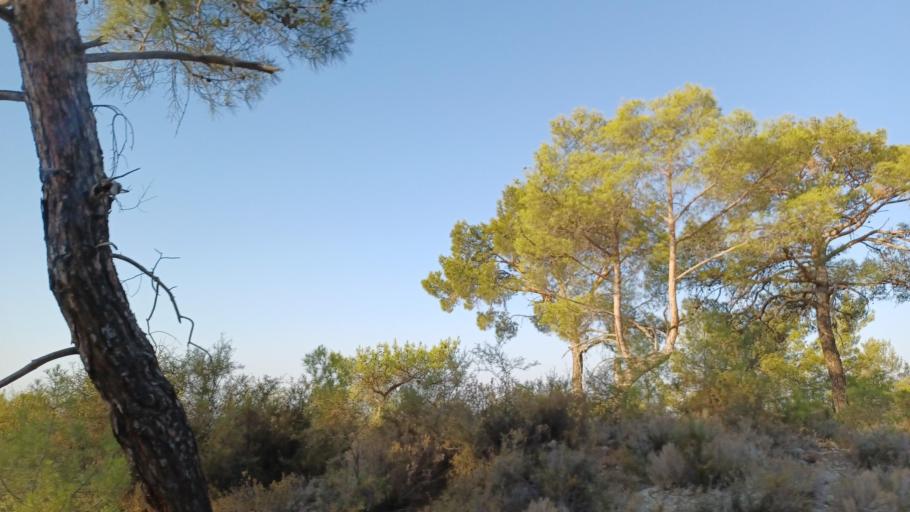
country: CY
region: Limassol
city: Pissouri
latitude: 34.7267
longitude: 32.6801
